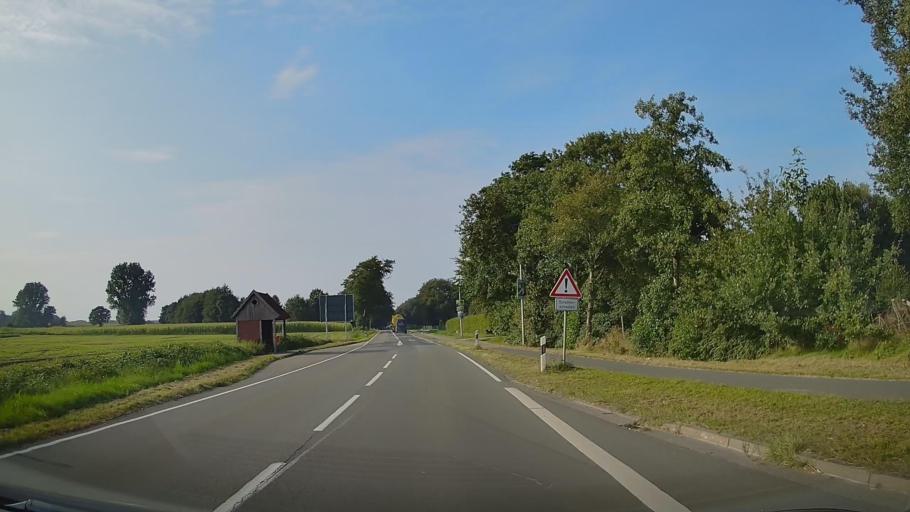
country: DE
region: Lower Saxony
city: Friesoythe
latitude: 53.1099
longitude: 7.8301
